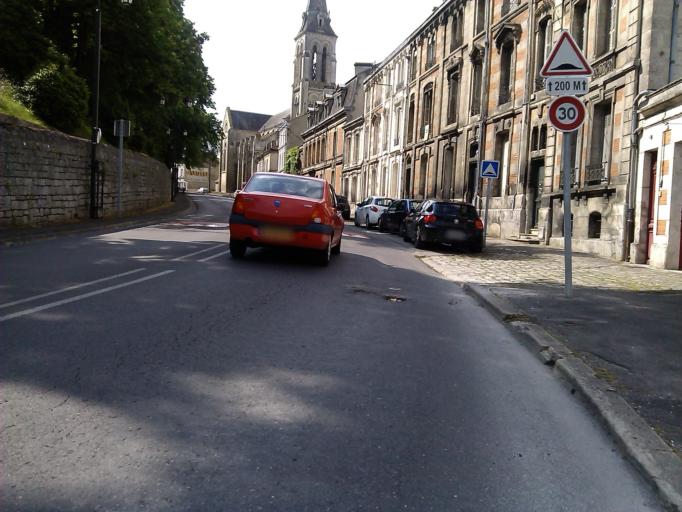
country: FR
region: Poitou-Charentes
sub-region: Departement de la Charente
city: Angouleme
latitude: 45.6519
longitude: 0.1453
